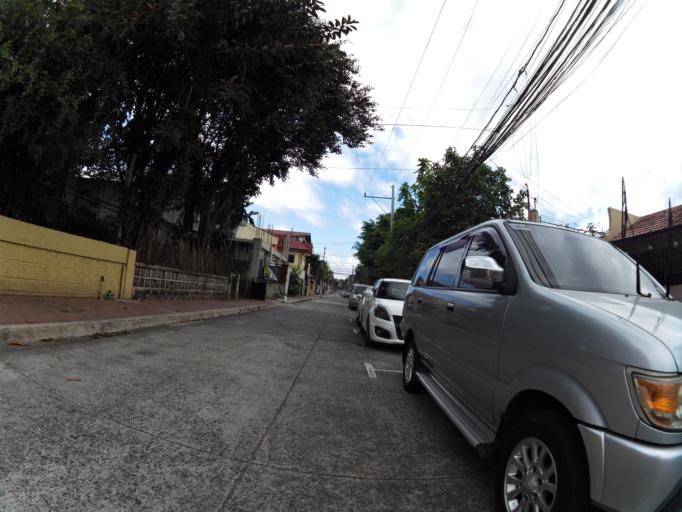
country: PH
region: Calabarzon
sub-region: Province of Rizal
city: Antipolo
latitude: 14.6404
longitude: 121.1140
